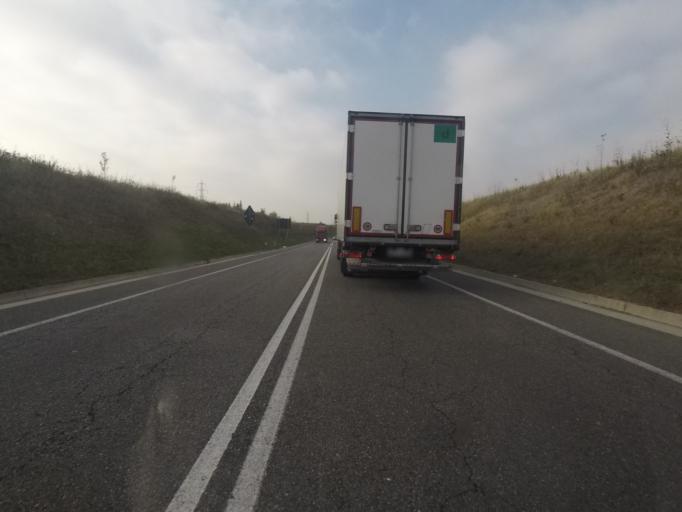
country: IT
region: Lombardy
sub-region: Provincia di Monza e Brianza
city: Burago di Molgora
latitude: 45.6077
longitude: 9.3821
